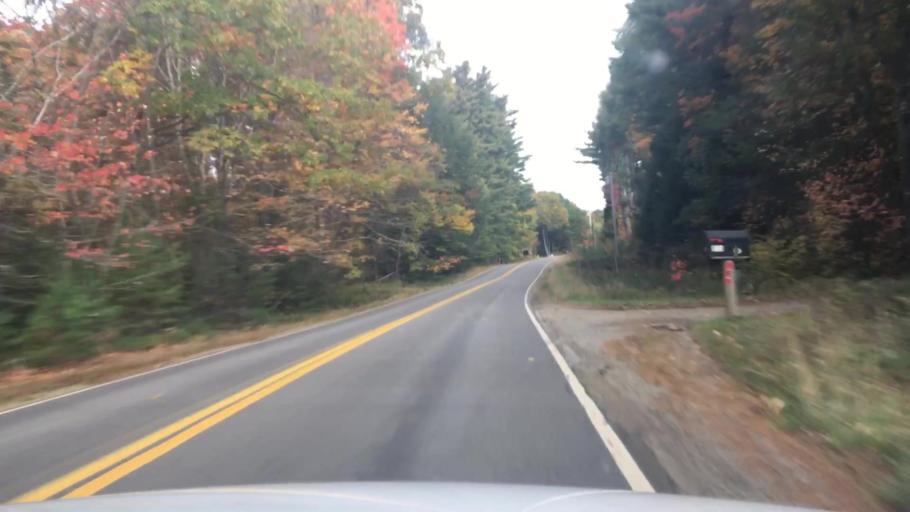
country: US
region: Maine
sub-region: Waldo County
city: Searsmont
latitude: 44.4219
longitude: -69.1420
